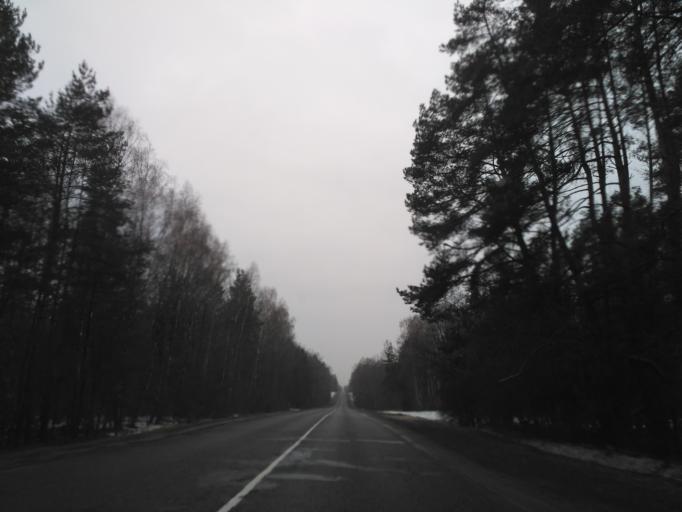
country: BY
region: Minsk
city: Snow
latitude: 53.2301
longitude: 26.2026
